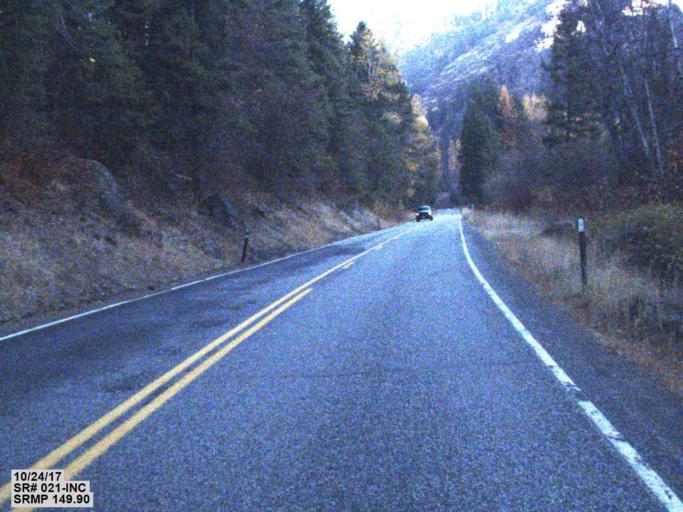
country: US
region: Washington
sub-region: Ferry County
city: Republic
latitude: 48.5039
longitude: -118.7407
